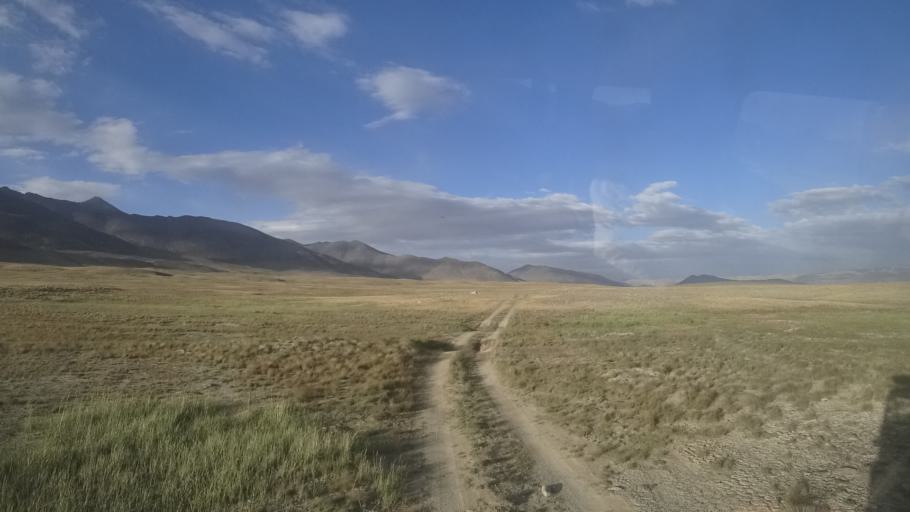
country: TJ
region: Gorno-Badakhshan
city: Murghob
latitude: 37.4709
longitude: 73.9599
